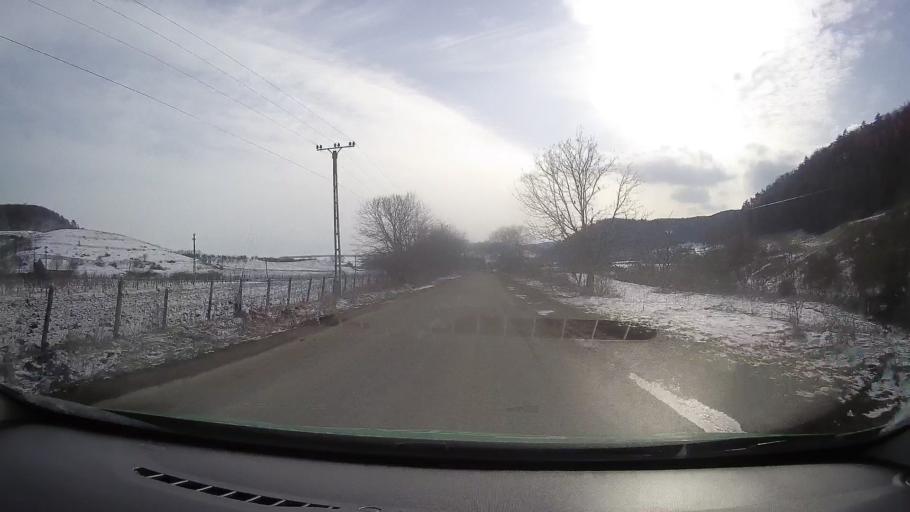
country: RO
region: Mures
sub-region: Comuna Apold
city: Apold
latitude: 46.1377
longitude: 24.8200
